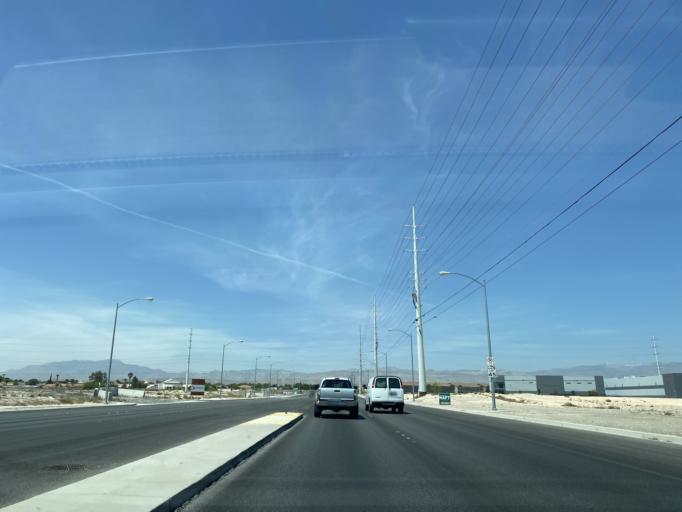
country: US
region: Nevada
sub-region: Clark County
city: Spring Valley
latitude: 36.0863
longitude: -115.2089
